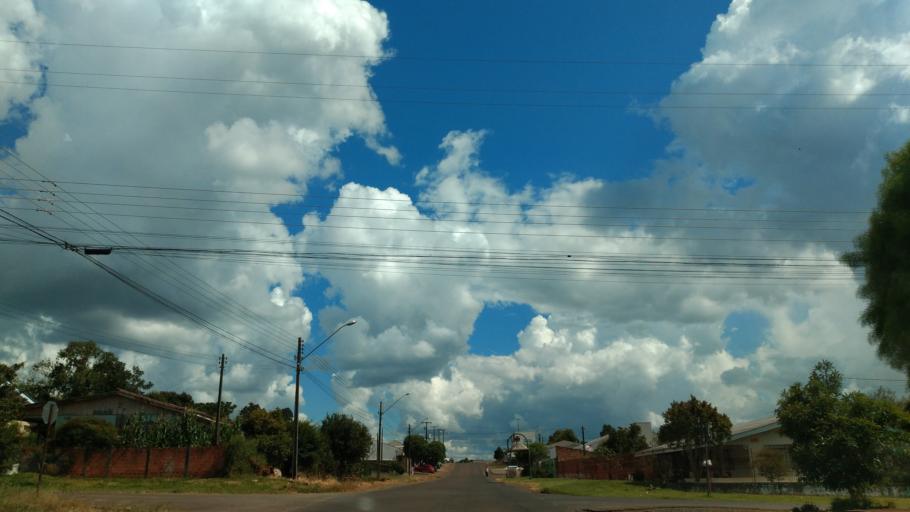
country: BR
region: Parana
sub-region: Guarapuava
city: Guarapuava
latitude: -25.4100
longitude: -51.4923
